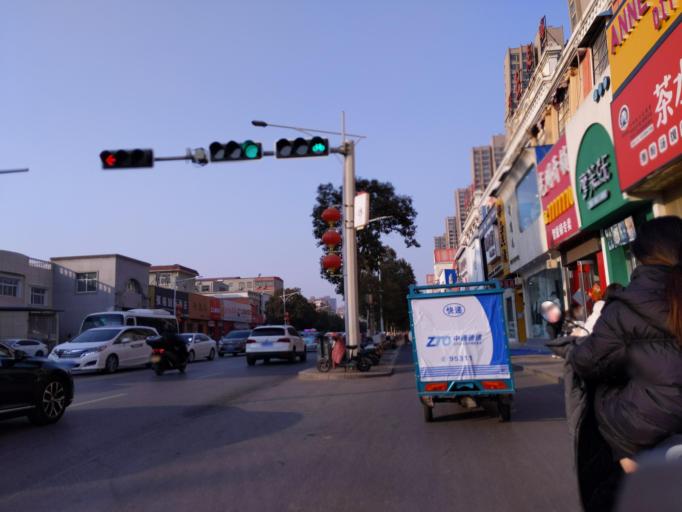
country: CN
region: Henan Sheng
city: Puyang
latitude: 35.7724
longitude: 115.0328
